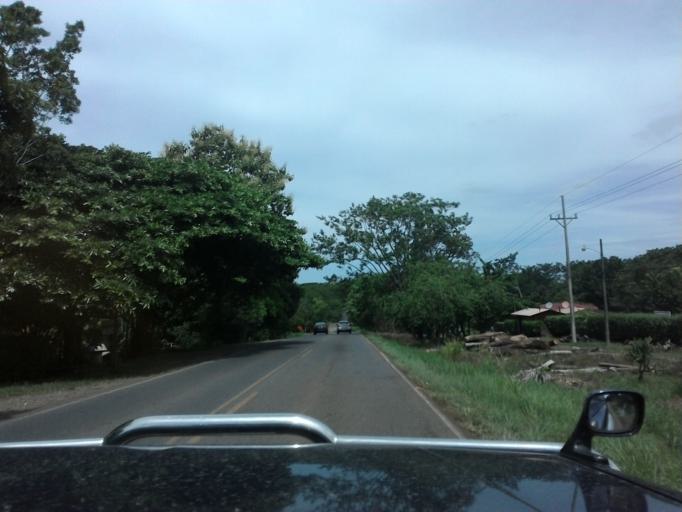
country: CR
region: Puntarenas
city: Esparza
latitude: 10.0039
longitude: -84.6342
